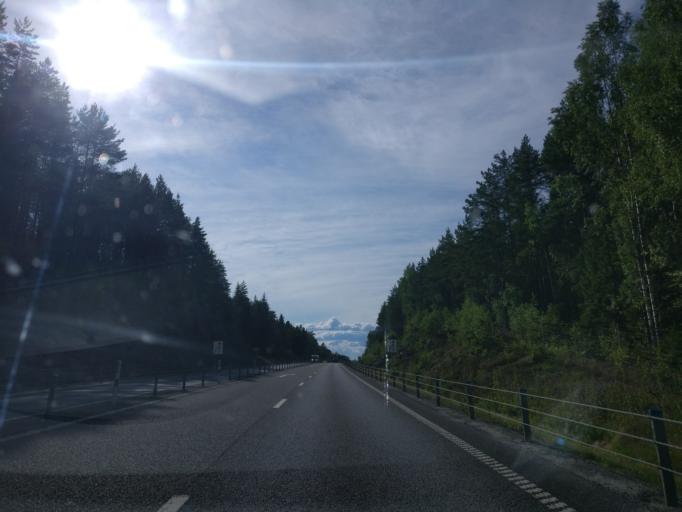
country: SE
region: Vaermland
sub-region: Arvika Kommun
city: Arvika
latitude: 59.6463
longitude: 12.7018
